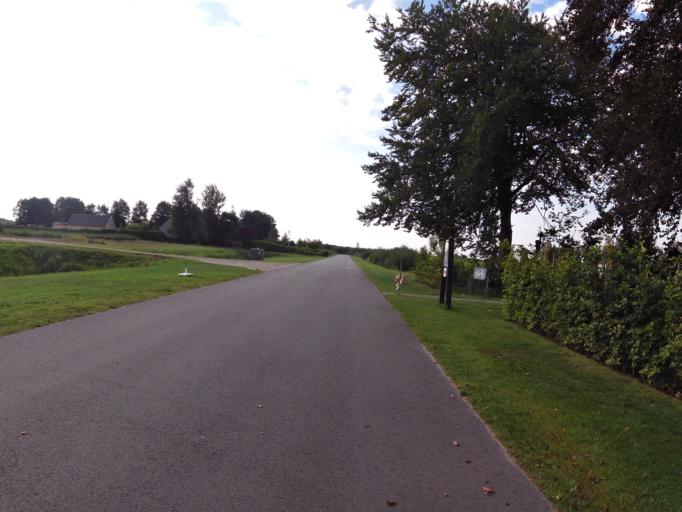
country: NL
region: Drenthe
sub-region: Gemeente Emmen
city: Klazienaveen
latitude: 52.7031
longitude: 7.0450
